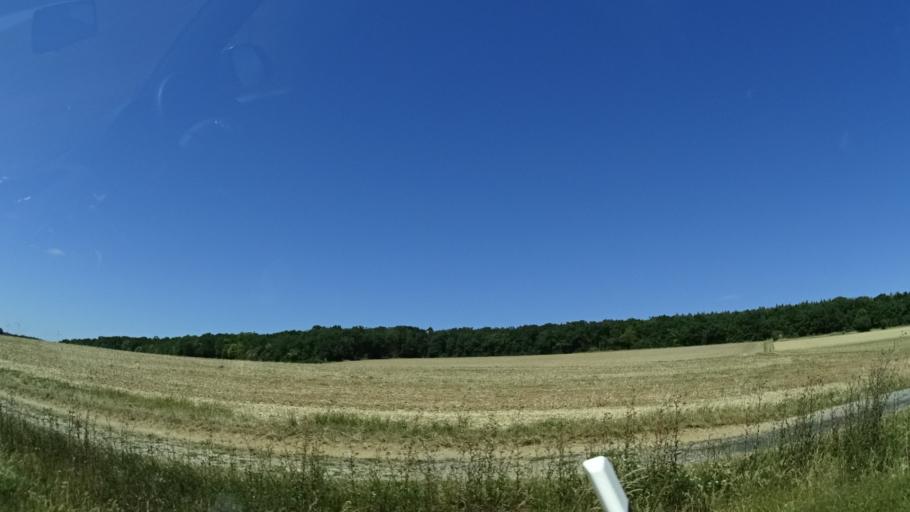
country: DE
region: Bavaria
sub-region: Regierungsbezirk Unterfranken
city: Rimpar
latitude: 49.8643
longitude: 9.9354
